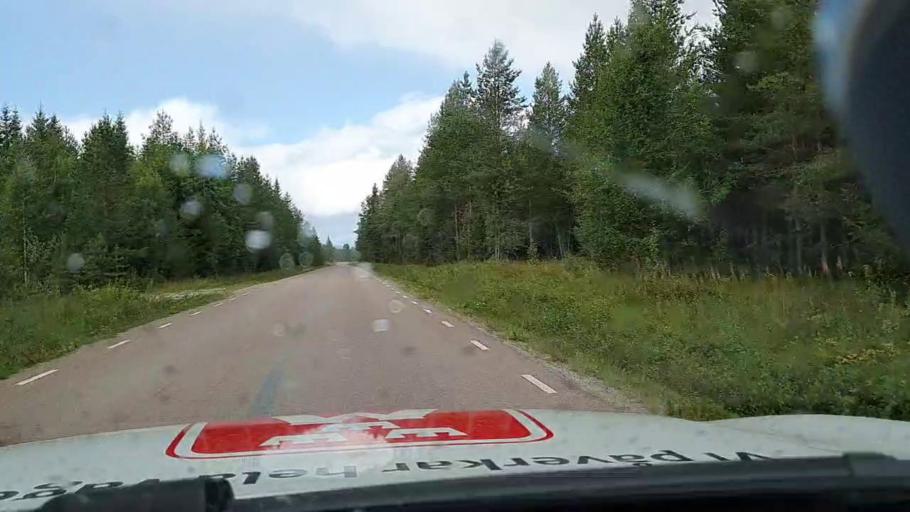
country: SE
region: Jaemtland
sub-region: Stroemsunds Kommun
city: Stroemsund
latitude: 63.8740
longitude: 15.3635
